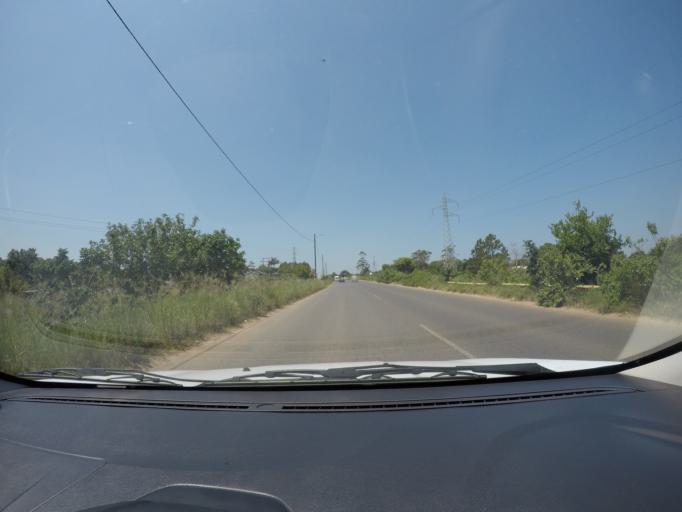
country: ZA
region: KwaZulu-Natal
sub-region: uThungulu District Municipality
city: eSikhawini
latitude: -28.8477
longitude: 31.9297
